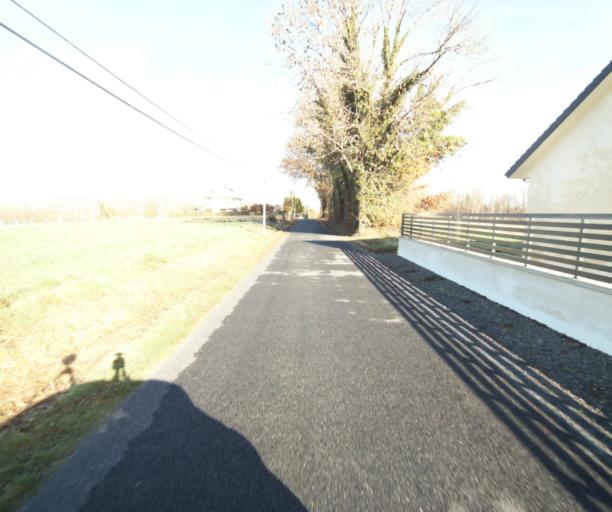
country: FR
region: Limousin
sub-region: Departement de la Correze
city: Laguenne
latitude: 45.2418
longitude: 1.7556
